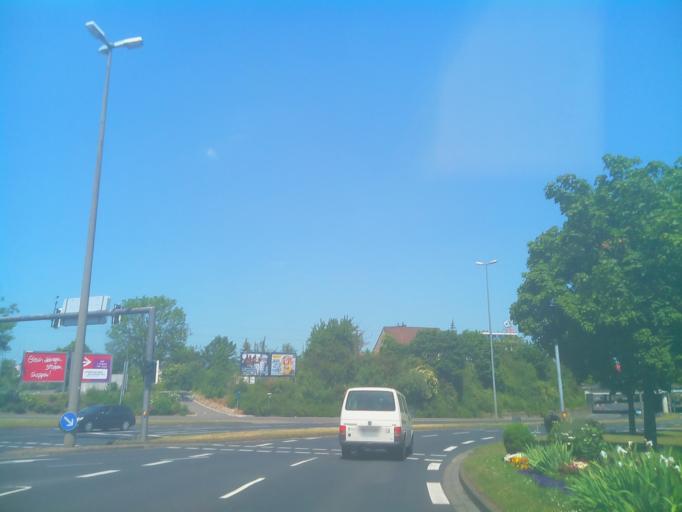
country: DE
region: Bavaria
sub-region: Regierungsbezirk Unterfranken
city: Schweinfurt
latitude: 50.0358
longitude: 10.2204
